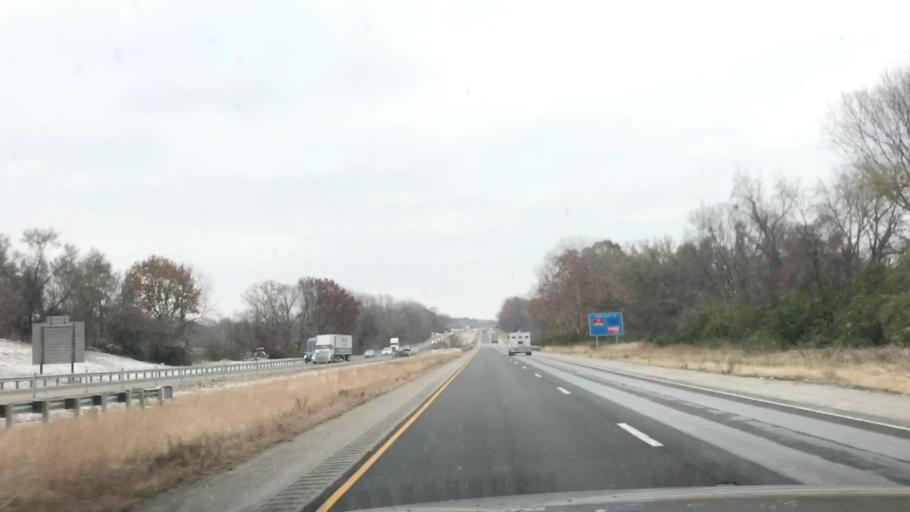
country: US
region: Illinois
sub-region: Madison County
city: Glen Carbon
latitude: 38.7567
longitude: -89.9843
